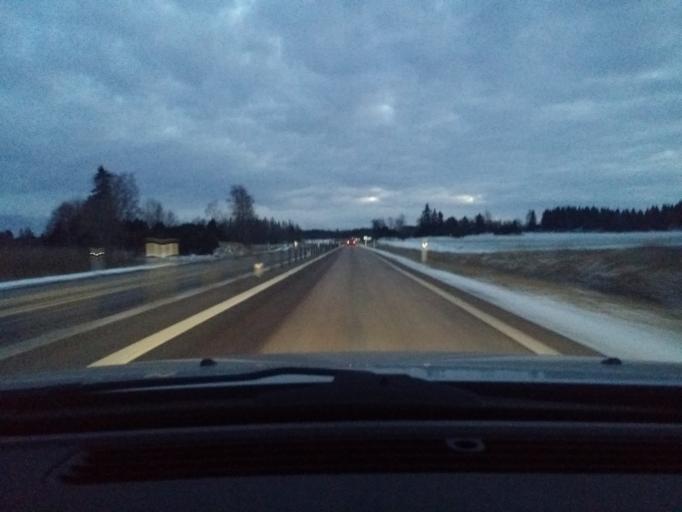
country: SE
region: Uppsala
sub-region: Enkopings Kommun
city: Orsundsbro
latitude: 59.6860
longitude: 17.2778
